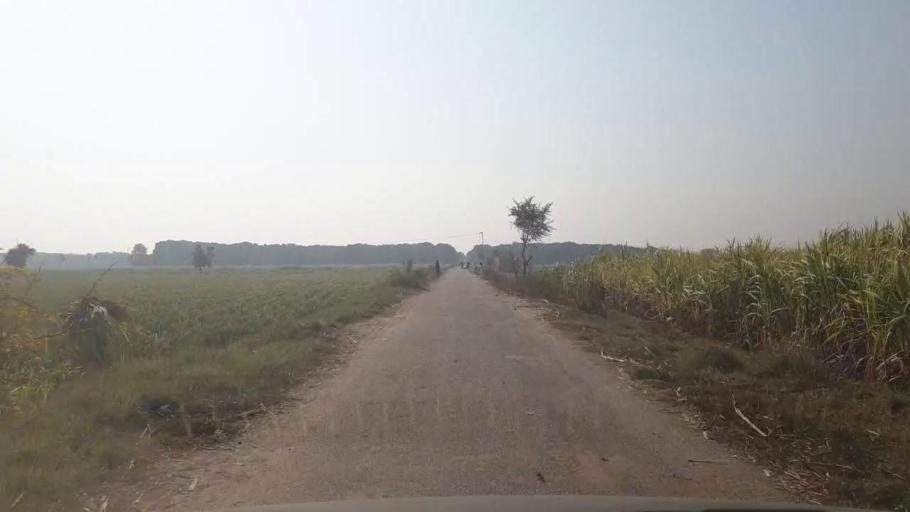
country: PK
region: Sindh
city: Tando Allahyar
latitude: 25.4747
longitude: 68.7617
